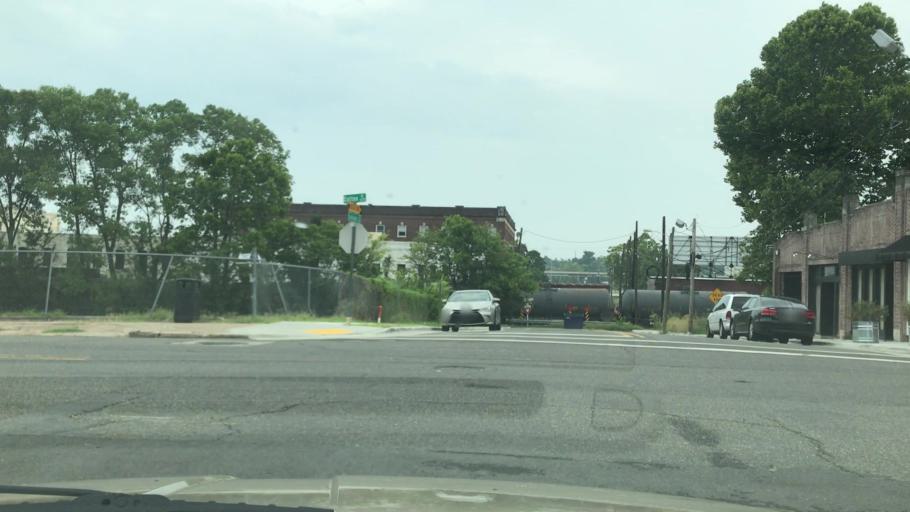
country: US
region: Louisiana
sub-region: Caddo Parish
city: Shreveport
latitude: 32.5091
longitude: -93.7492
